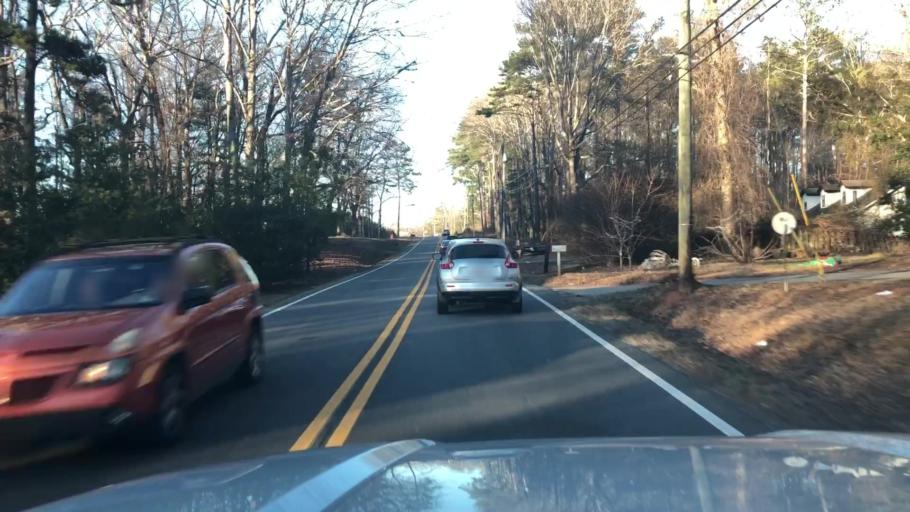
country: US
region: Georgia
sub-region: Cherokee County
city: Holly Springs
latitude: 34.2011
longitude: -84.5241
